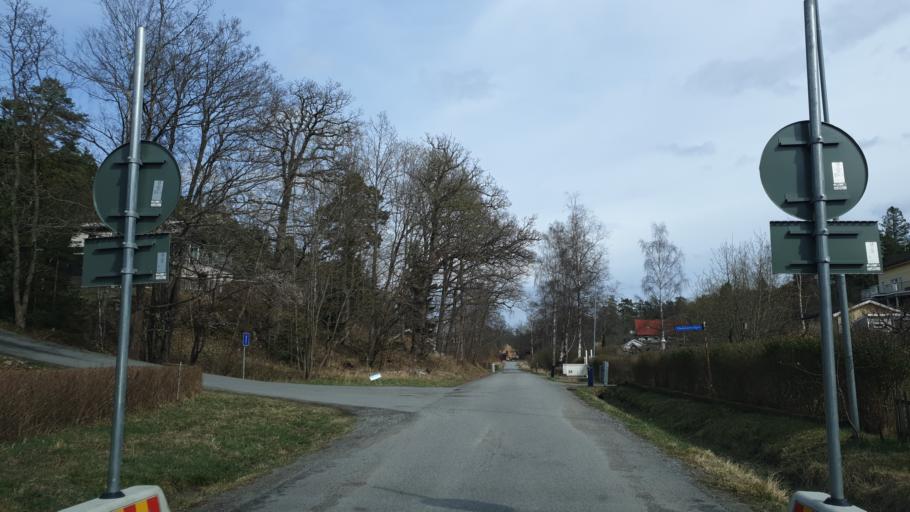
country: SE
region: Stockholm
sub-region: Nacka Kommun
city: Boo
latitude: 59.3287
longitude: 18.2931
